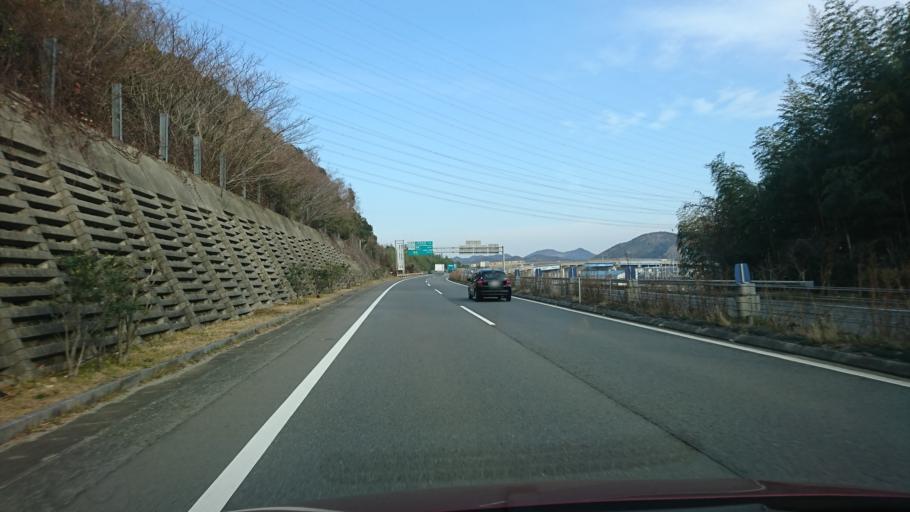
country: JP
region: Hyogo
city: Shirahamacho-usazakiminami
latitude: 34.8059
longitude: 134.7433
